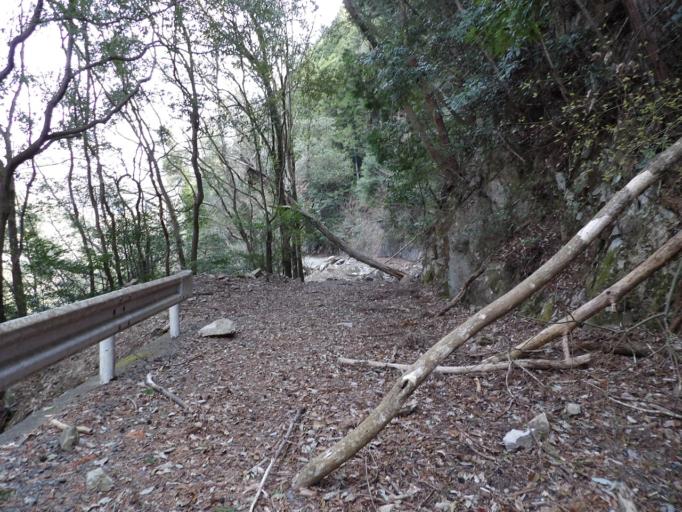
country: JP
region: Shizuoka
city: Mori
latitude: 35.1342
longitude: 137.8104
